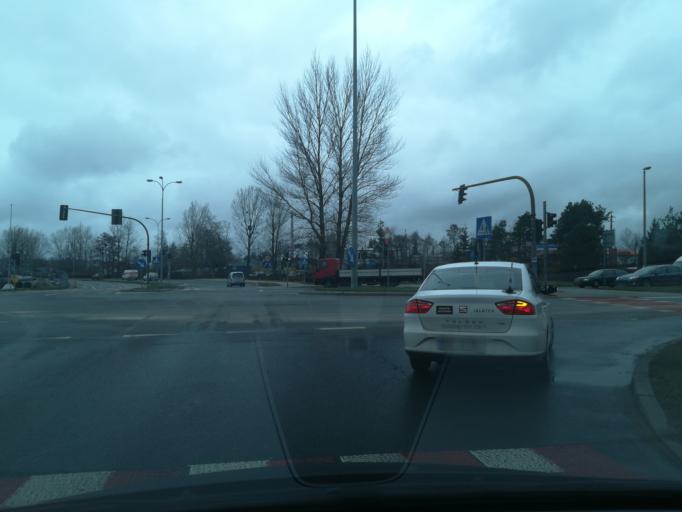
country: PL
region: Kujawsko-Pomorskie
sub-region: Powiat torunski
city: Lubicz Dolny
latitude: 53.0308
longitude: 18.7010
